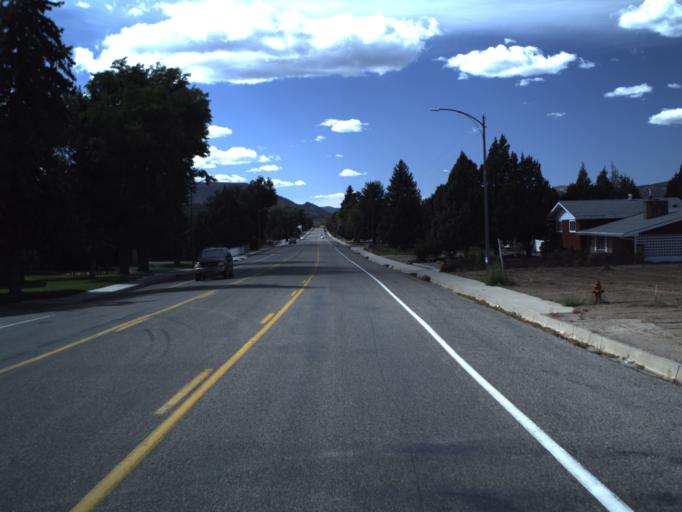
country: US
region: Utah
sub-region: Washington County
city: Enterprise
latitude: 37.5736
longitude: -113.7122
